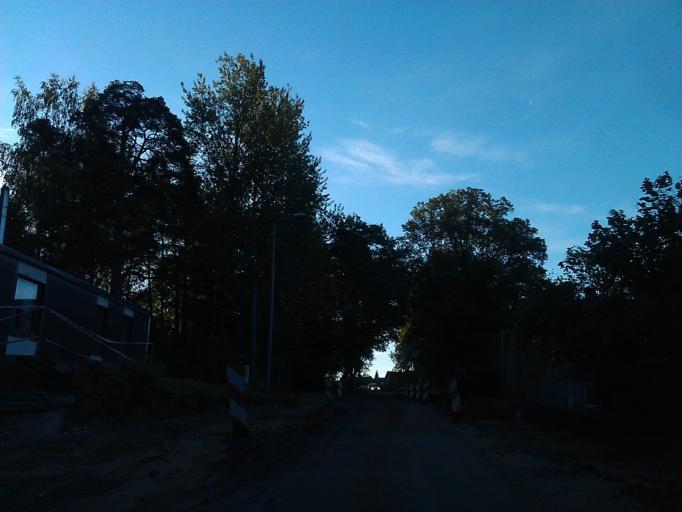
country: LV
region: Cesu Rajons
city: Cesis
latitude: 57.3081
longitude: 25.2366
